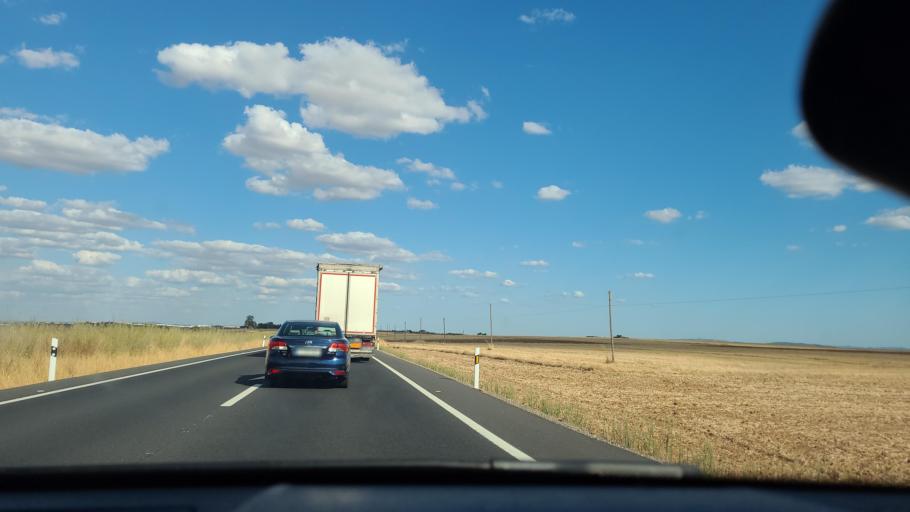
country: ES
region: Extremadura
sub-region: Provincia de Badajoz
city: Azuaga
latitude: 38.2636
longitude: -5.7379
